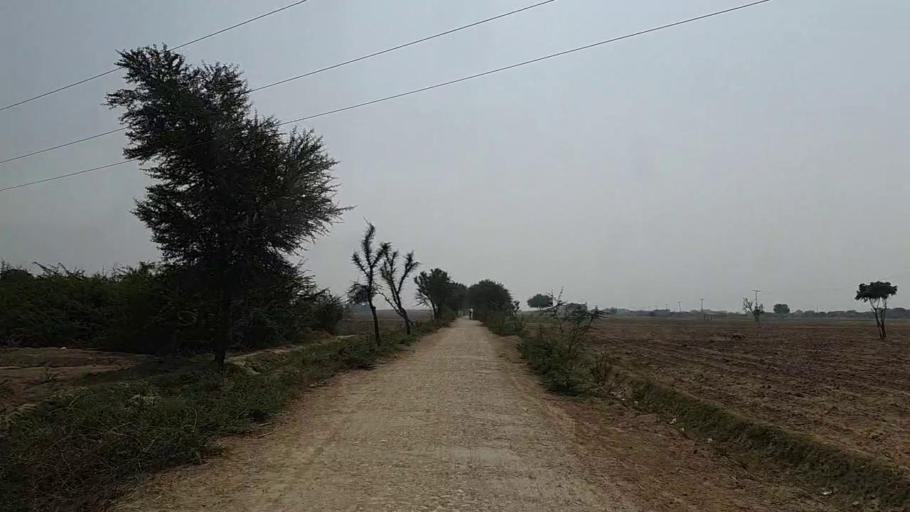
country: PK
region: Sindh
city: Naukot
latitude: 24.8210
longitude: 69.3596
